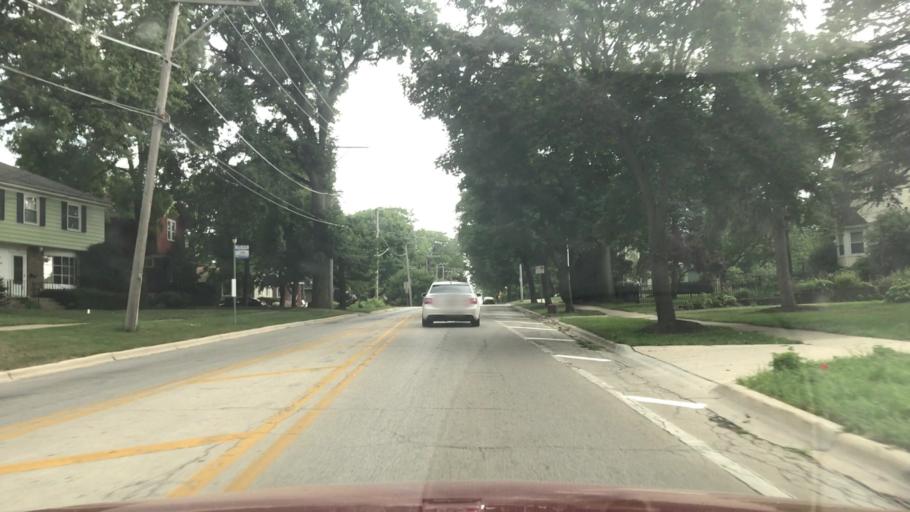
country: US
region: Illinois
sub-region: DuPage County
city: Wheaton
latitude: 41.8664
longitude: -88.0920
